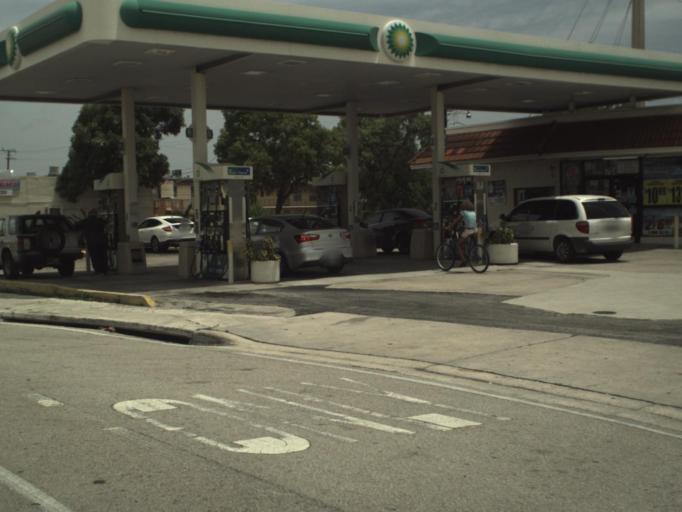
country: US
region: Florida
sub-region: Broward County
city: Hallandale Beach
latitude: 25.9932
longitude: -80.1425
